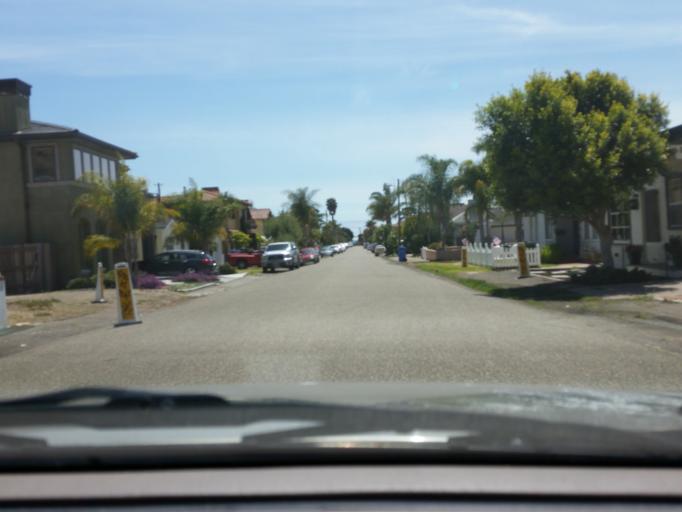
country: US
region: California
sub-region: San Luis Obispo County
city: Pismo Beach
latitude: 35.1561
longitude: -120.6718
